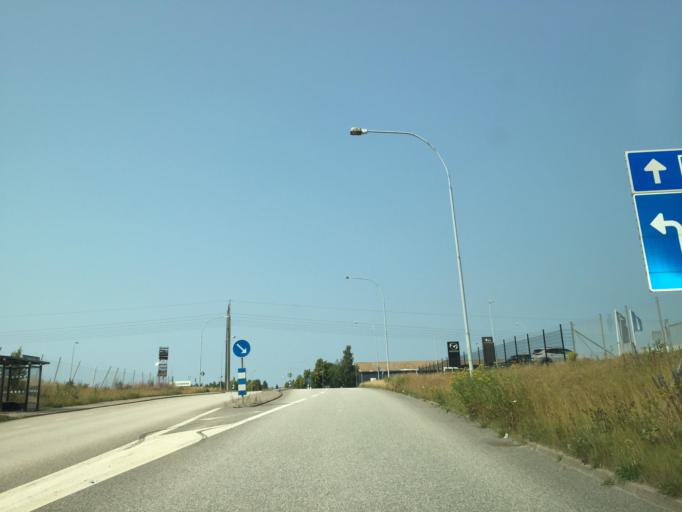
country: SE
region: Vaestra Goetaland
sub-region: Trollhattan
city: Trollhattan
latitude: 58.3392
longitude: 12.2541
